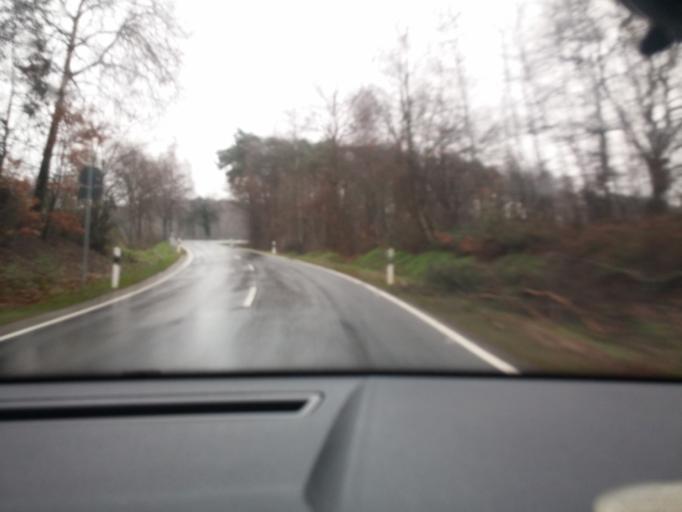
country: DE
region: Hesse
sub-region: Regierungsbezirk Darmstadt
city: Brensbach
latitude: 49.7598
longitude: 8.8996
